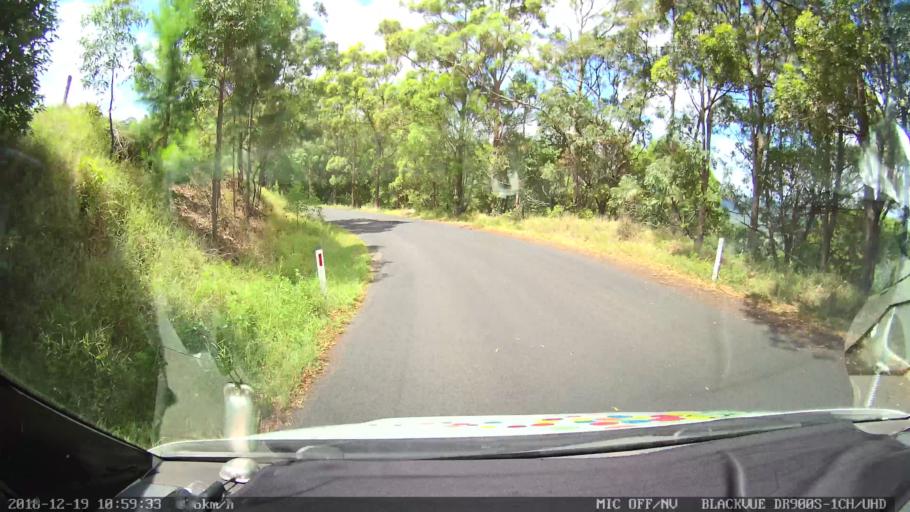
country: AU
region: New South Wales
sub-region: Lismore Municipality
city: Nimbin
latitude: -28.5967
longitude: 153.2616
